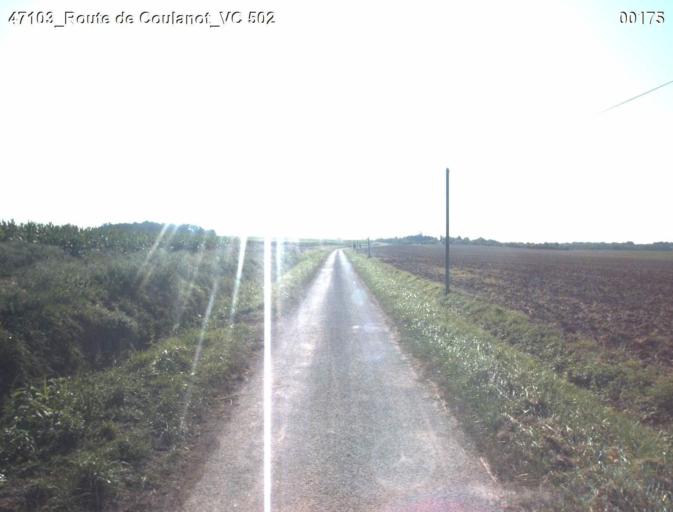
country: FR
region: Aquitaine
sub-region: Departement du Lot-et-Garonne
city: Nerac
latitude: 44.0758
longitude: 0.3313
